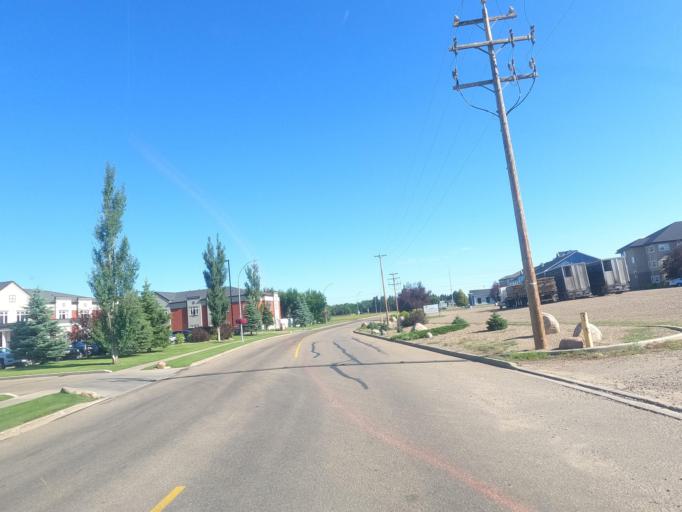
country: CA
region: Alberta
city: Brooks
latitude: 50.5828
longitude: -111.8998
